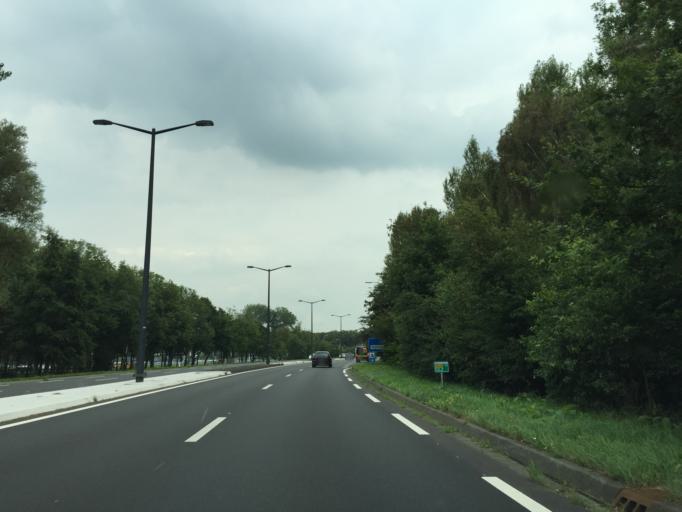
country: NL
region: South Holland
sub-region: Gemeente Leidschendam-Voorburg
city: Voorburg
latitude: 52.1127
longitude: 4.3409
